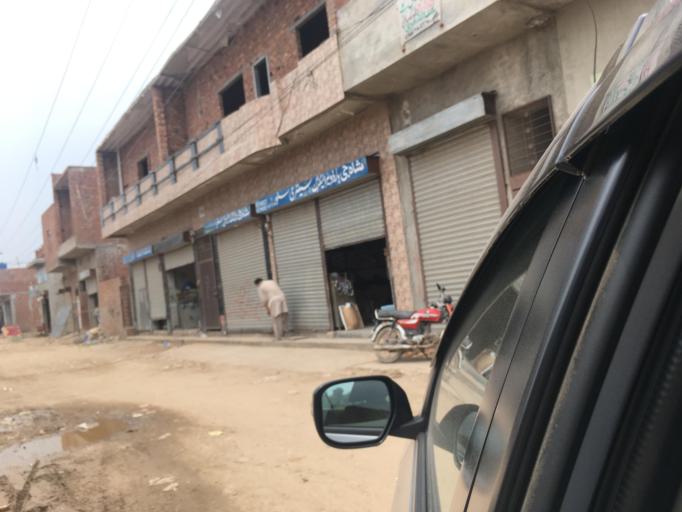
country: PK
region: Punjab
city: Lahore
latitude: 31.6122
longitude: 74.3544
